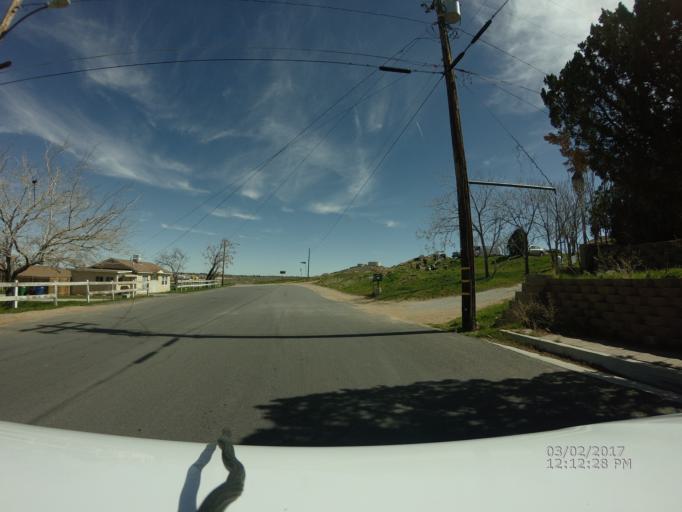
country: US
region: California
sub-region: Los Angeles County
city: Quartz Hill
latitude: 34.6473
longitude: -118.2104
